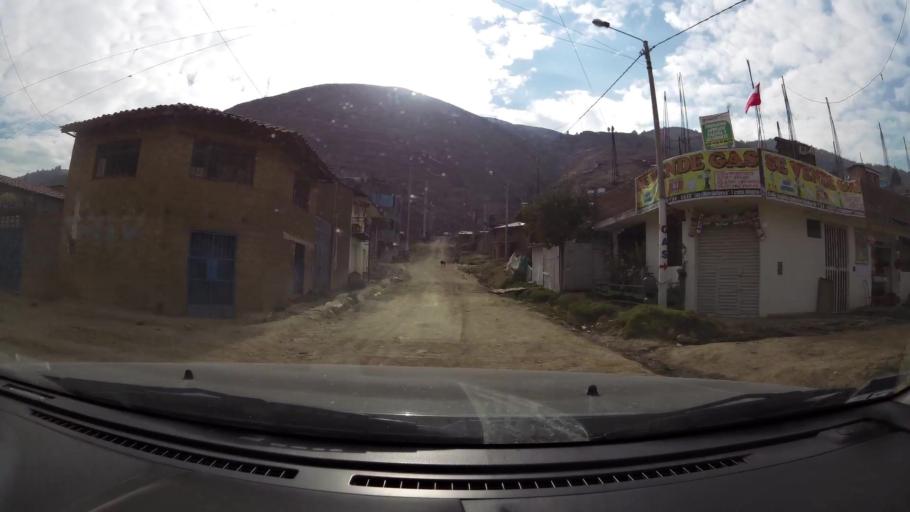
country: PE
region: Junin
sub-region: Provincia de Huancayo
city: Huancayo
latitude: -12.0516
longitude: -75.1865
